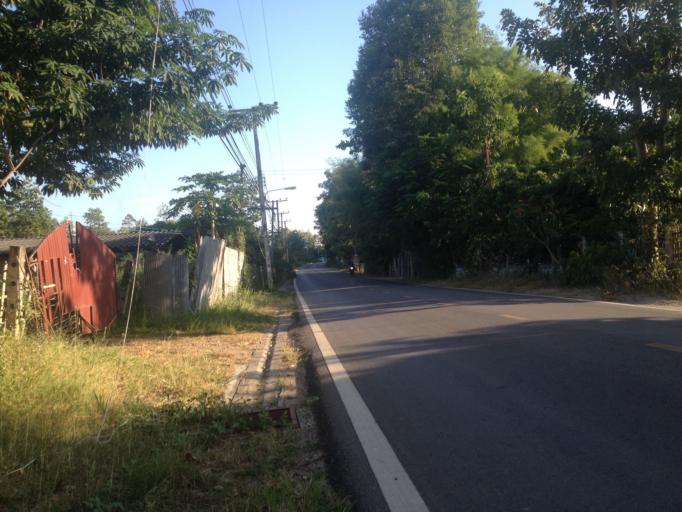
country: TH
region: Chiang Mai
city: San Pa Tong
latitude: 18.5837
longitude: 98.8645
